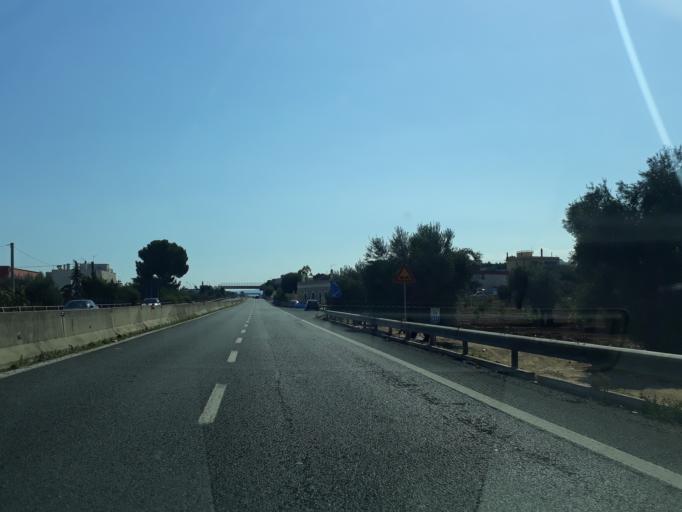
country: IT
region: Apulia
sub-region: Provincia di Brindisi
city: Fasano
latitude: 40.8941
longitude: 17.3310
